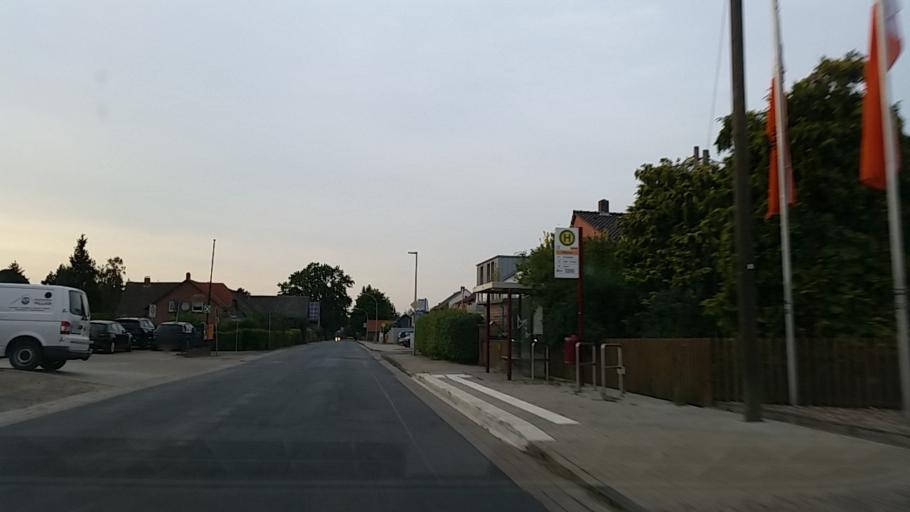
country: DE
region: Lower Saxony
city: Klein Schwulper
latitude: 52.3474
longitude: 10.4586
